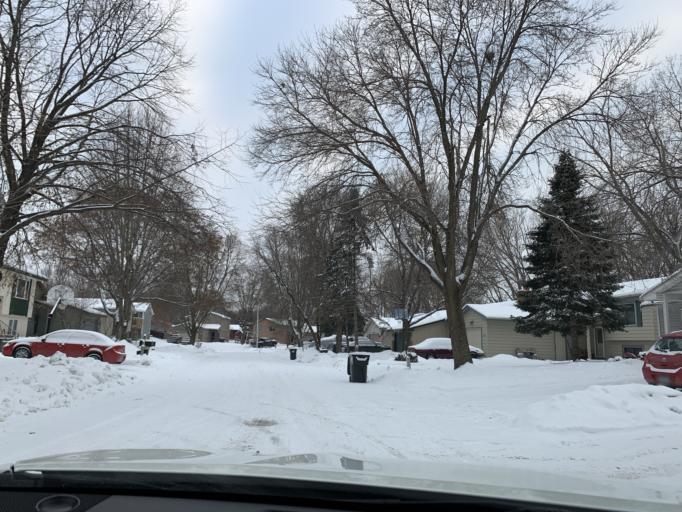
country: US
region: Minnesota
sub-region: Anoka County
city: Coon Rapids
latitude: 45.1617
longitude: -93.2931
